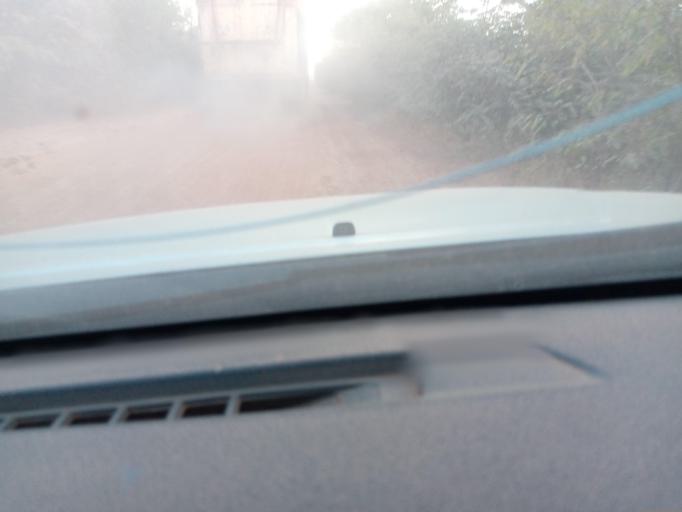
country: ML
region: Koulikoro
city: Dioila
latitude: 12.1591
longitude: -6.1717
